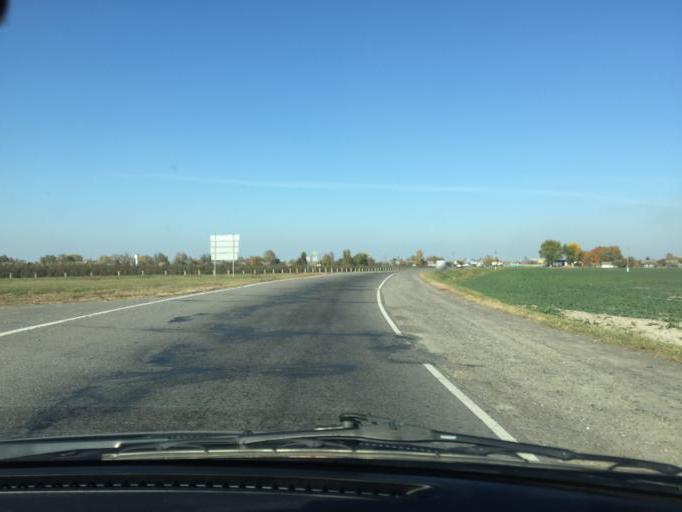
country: BY
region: Gomel
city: Turaw
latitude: 52.0578
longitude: 27.8201
